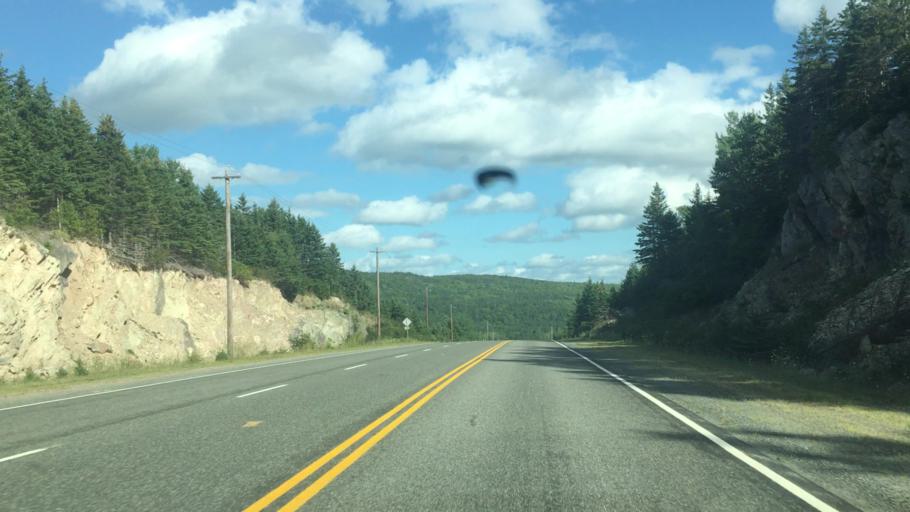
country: CA
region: Nova Scotia
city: Sydney
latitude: 45.8145
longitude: -60.6835
